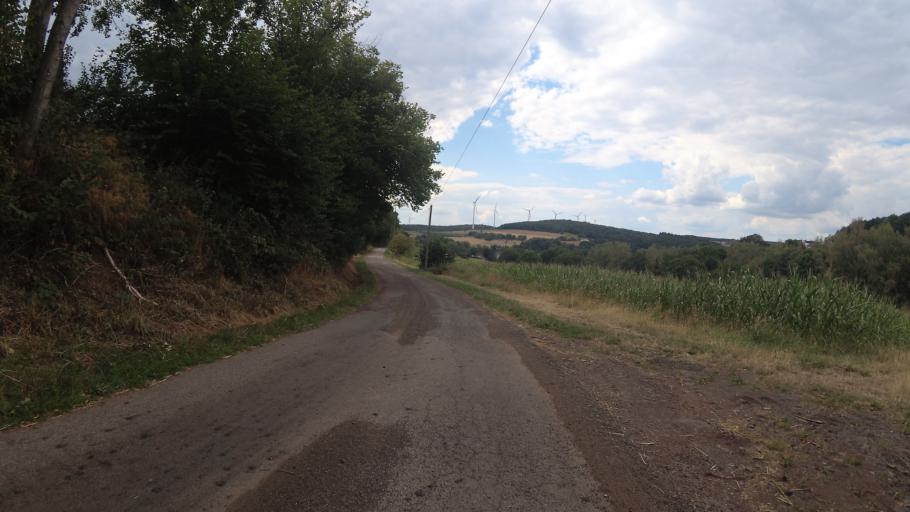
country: DE
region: Rheinland-Pfalz
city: Breitenbach
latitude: 49.4343
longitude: 7.2451
